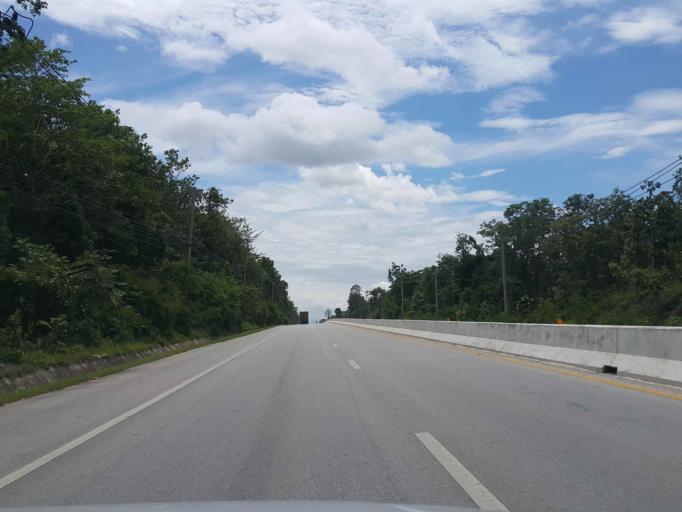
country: TH
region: Sukhothai
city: Ban Dan Lan Hoi
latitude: 17.0253
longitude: 99.6145
